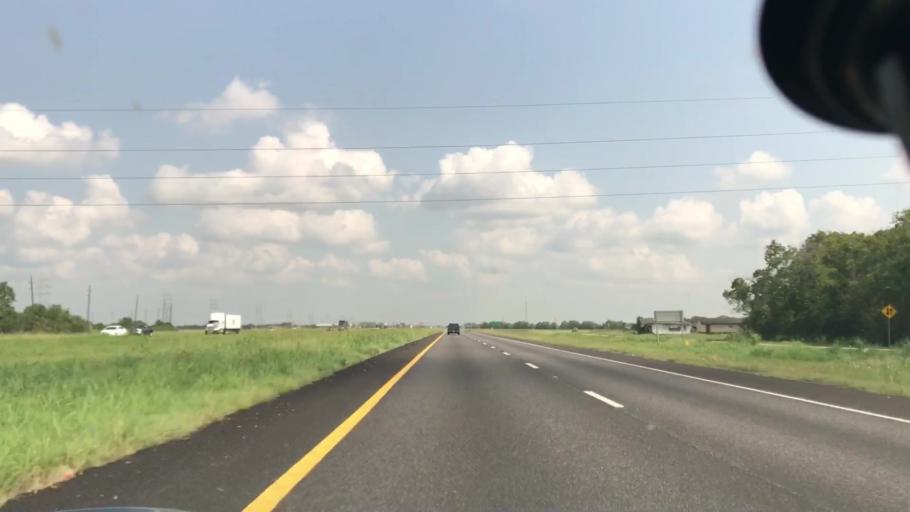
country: US
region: Texas
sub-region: Brazoria County
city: Rosharon
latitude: 29.4049
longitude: -95.4268
